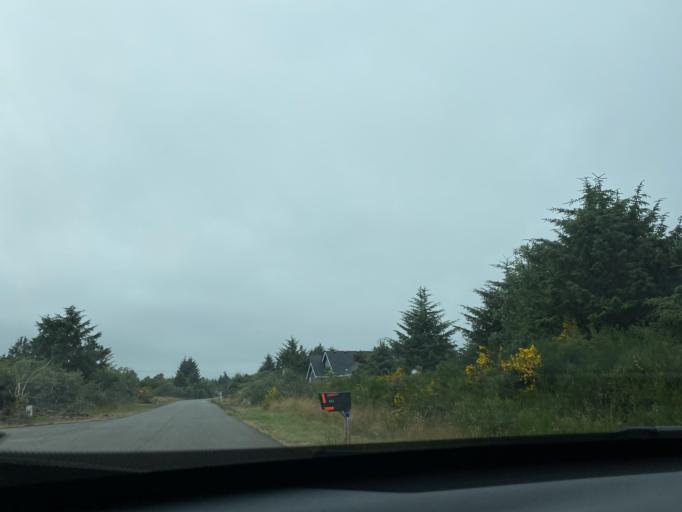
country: US
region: Washington
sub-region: Grays Harbor County
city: Ocean Shores
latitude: 46.9510
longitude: -124.1430
